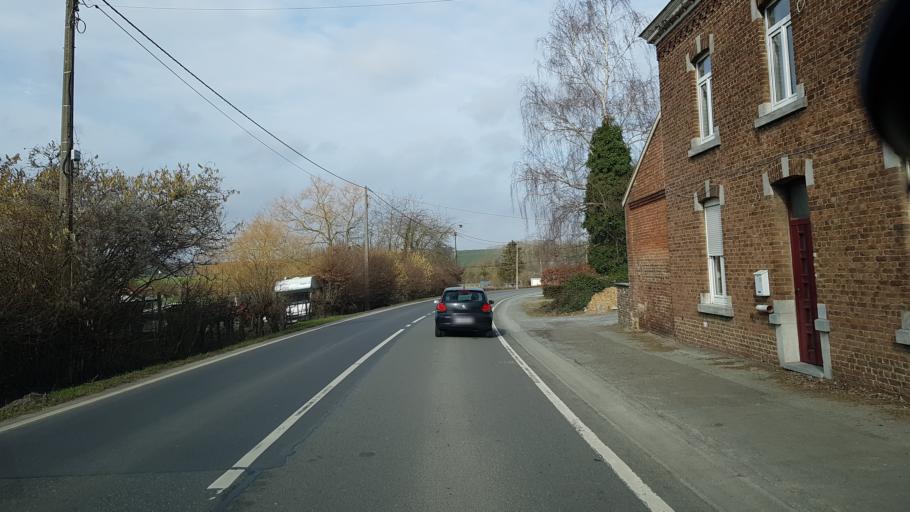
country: BE
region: Wallonia
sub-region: Province de Liege
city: Braives
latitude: 50.6041
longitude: 5.1928
